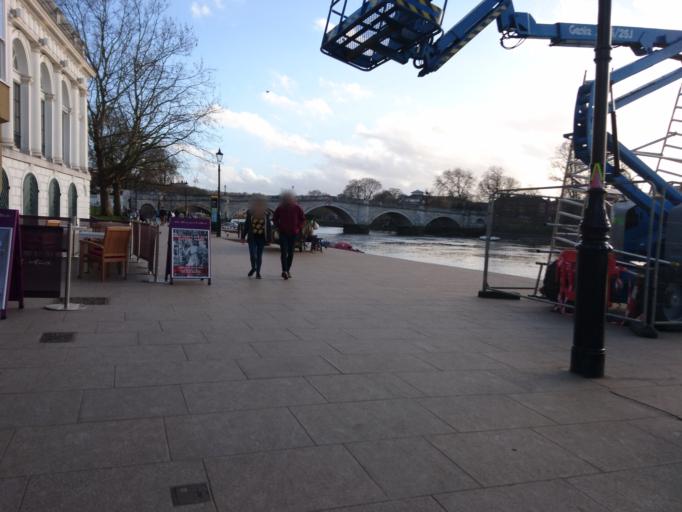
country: GB
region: England
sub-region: Greater London
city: Richmond
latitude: 51.4588
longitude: -0.3080
